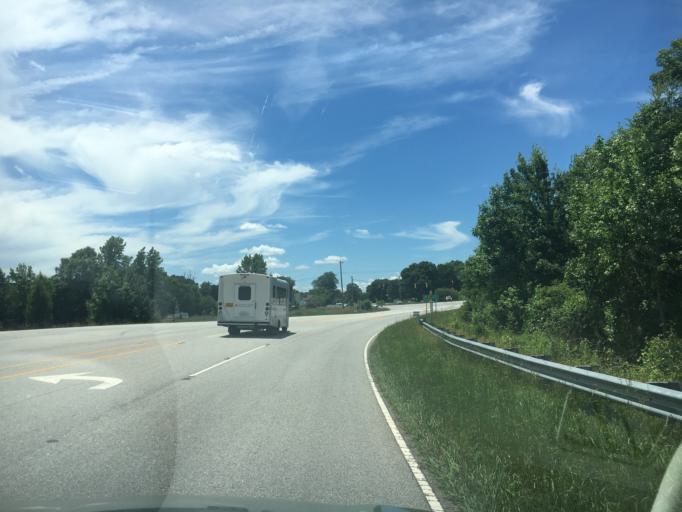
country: US
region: South Carolina
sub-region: Spartanburg County
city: Duncan
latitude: 34.8525
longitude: -82.1456
